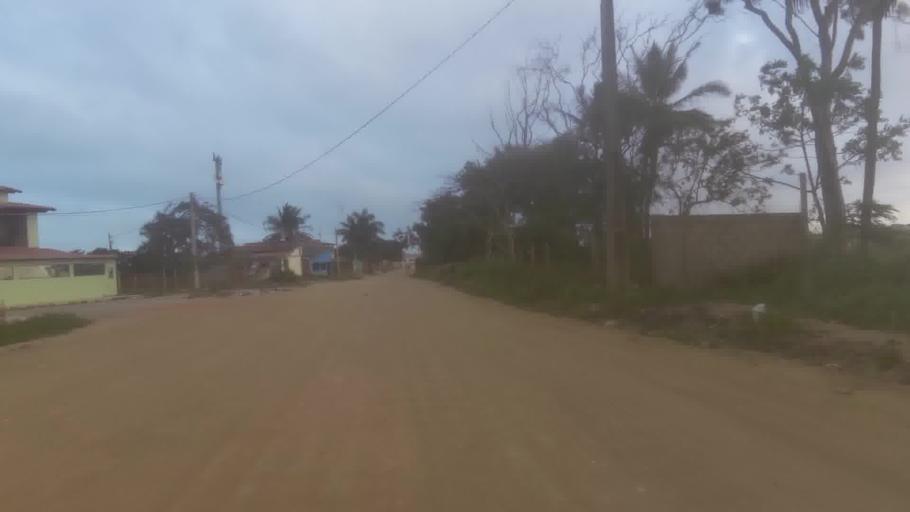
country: BR
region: Espirito Santo
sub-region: Marataizes
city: Marataizes
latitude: -21.0368
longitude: -40.8237
